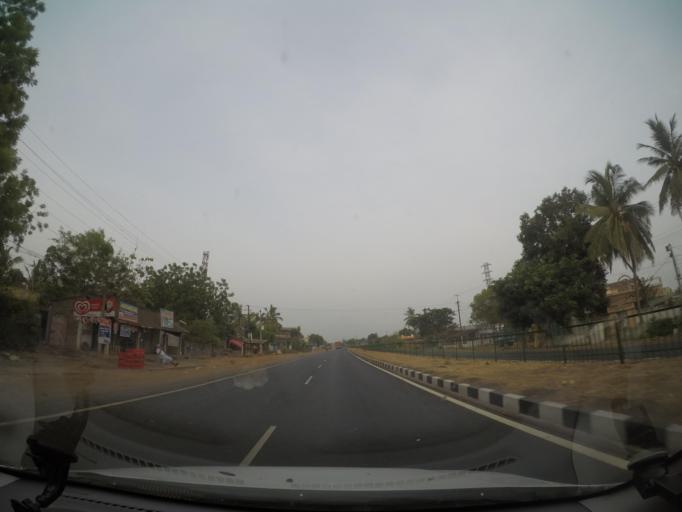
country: IN
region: Andhra Pradesh
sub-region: Krishna
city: Gannavaram
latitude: 16.6104
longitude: 80.9111
